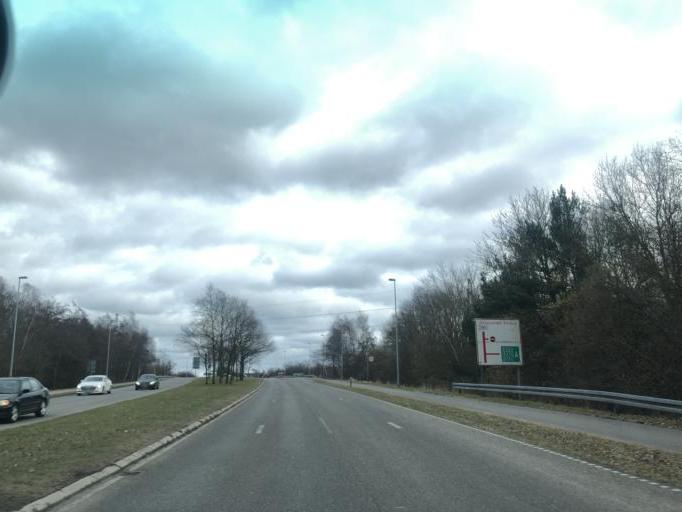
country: DK
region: Capital Region
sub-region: Vallensbaek Kommune
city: Vallensbaek
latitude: 55.6301
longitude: 12.3798
